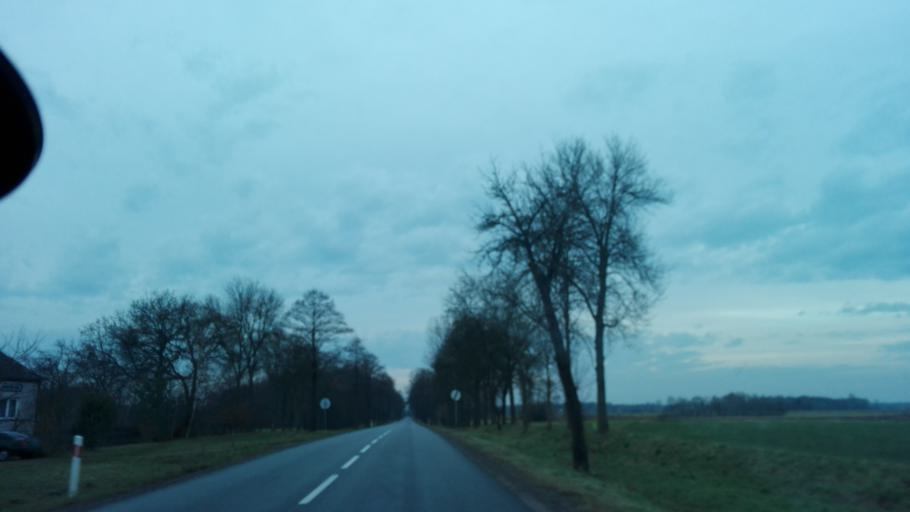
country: PL
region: Lublin Voivodeship
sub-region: Powiat radzynski
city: Wohyn
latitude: 51.7803
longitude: 22.7557
